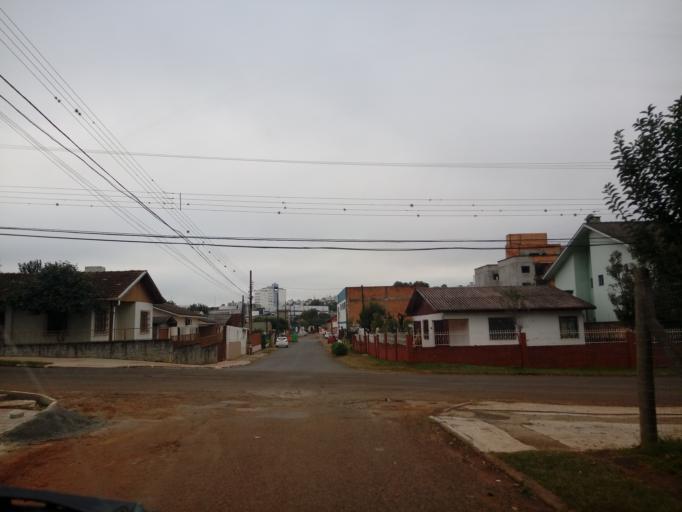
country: BR
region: Santa Catarina
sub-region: Chapeco
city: Chapeco
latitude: -27.0871
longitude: -52.6256
